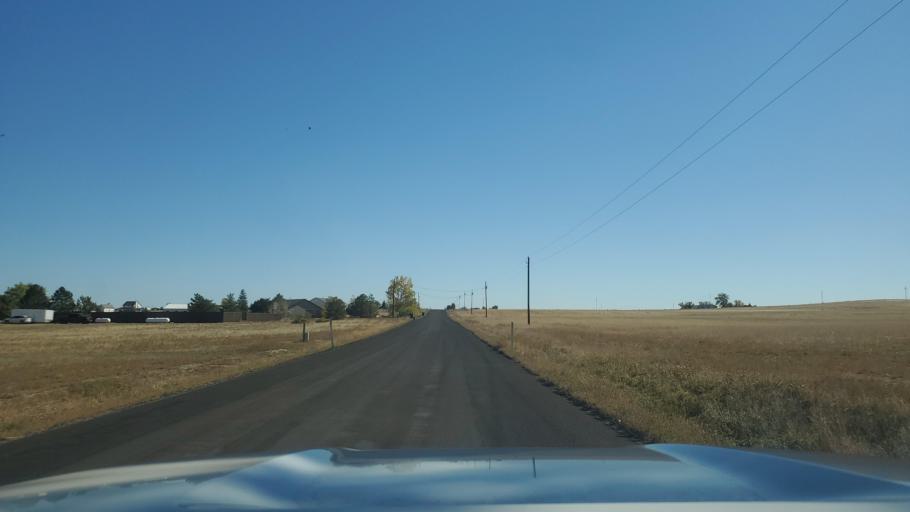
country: US
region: Colorado
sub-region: Adams County
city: Bennett
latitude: 39.7600
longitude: -104.3907
